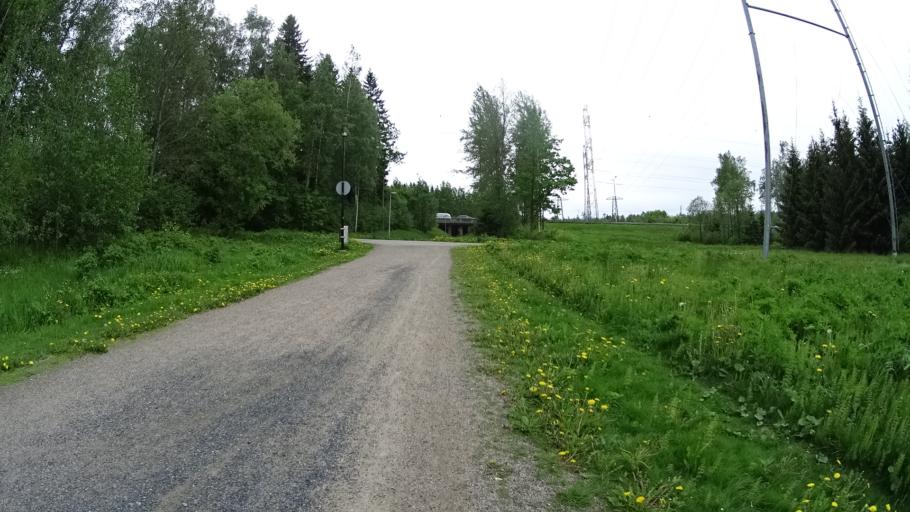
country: FI
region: Uusimaa
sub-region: Helsinki
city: Vantaa
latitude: 60.2805
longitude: 25.0574
